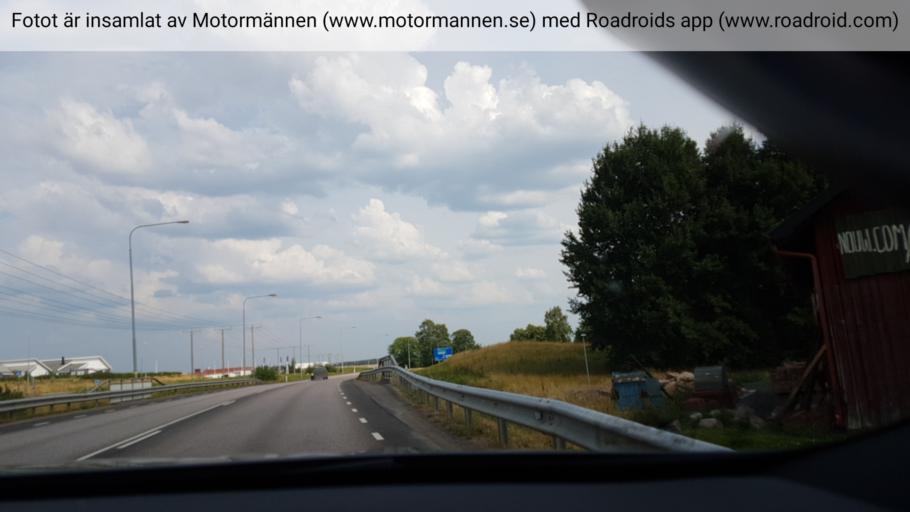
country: SE
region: Vaestra Goetaland
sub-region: Skara Kommun
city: Skara
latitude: 58.3938
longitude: 13.4545
